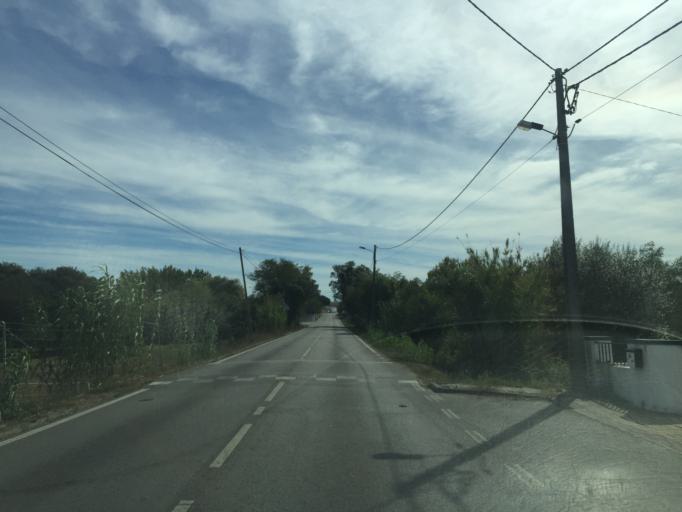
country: PT
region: Coimbra
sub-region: Figueira da Foz
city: Lavos
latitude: 40.1069
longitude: -8.8372
